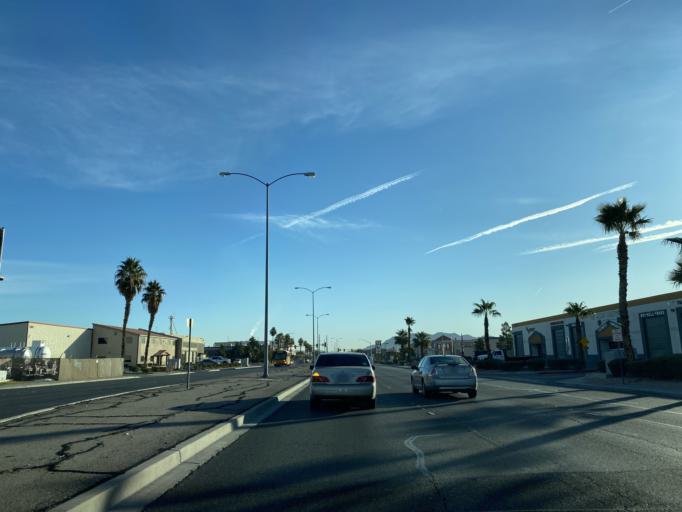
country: US
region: Nevada
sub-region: Clark County
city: Sunrise Manor
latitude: 36.2403
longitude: -115.0917
